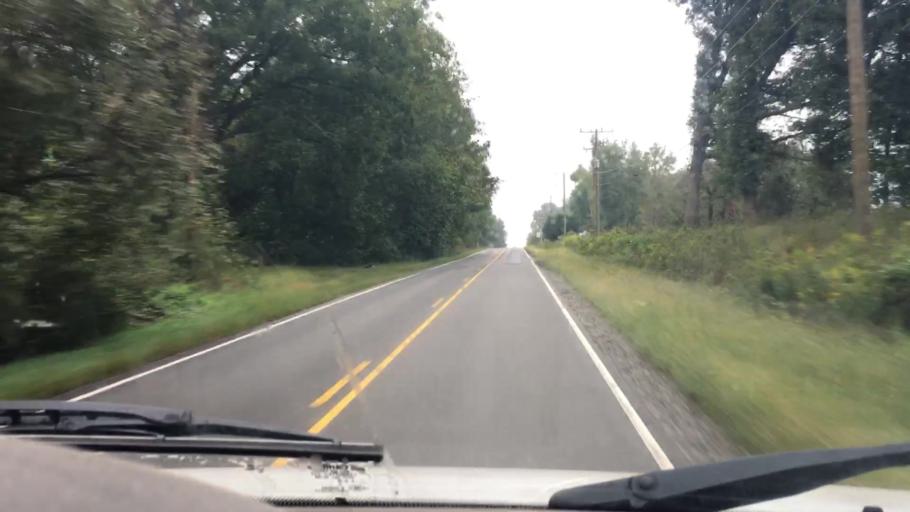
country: US
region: North Carolina
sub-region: Iredell County
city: Mooresville
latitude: 35.6257
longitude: -80.7811
